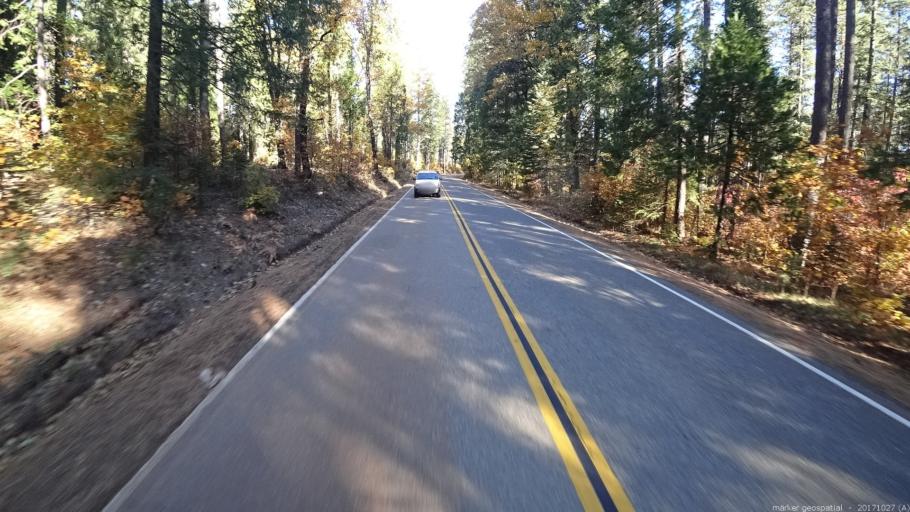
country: US
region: California
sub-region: Shasta County
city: Burney
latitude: 40.9384
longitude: -121.9493
